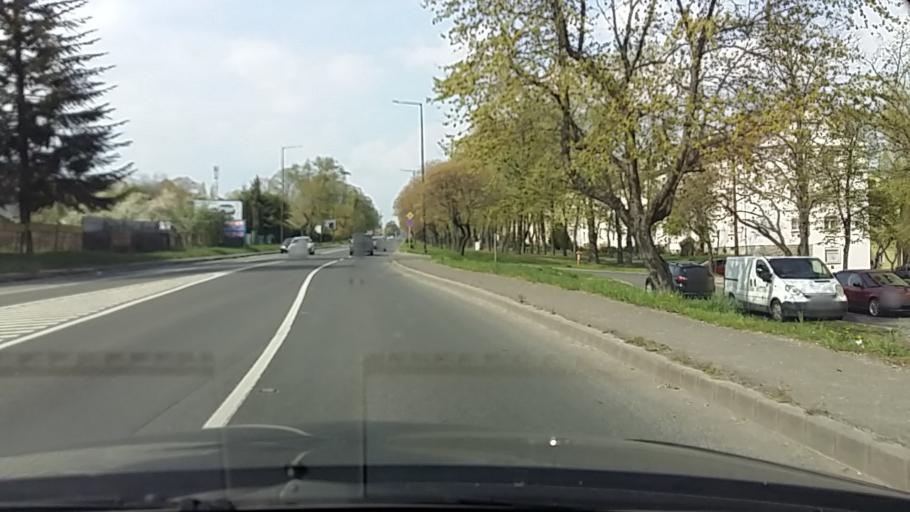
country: HU
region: Baranya
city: Pecs
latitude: 46.0981
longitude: 18.2667
